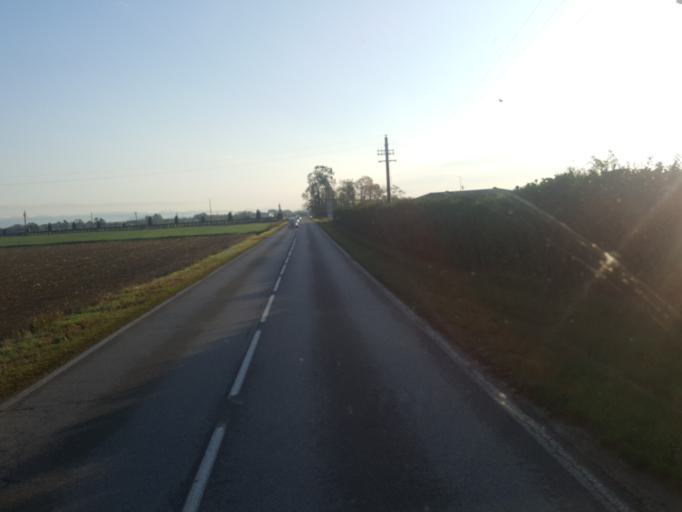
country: IT
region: Lombardy
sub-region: Provincia di Bergamo
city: Pagazzano
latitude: 45.5327
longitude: 9.6827
